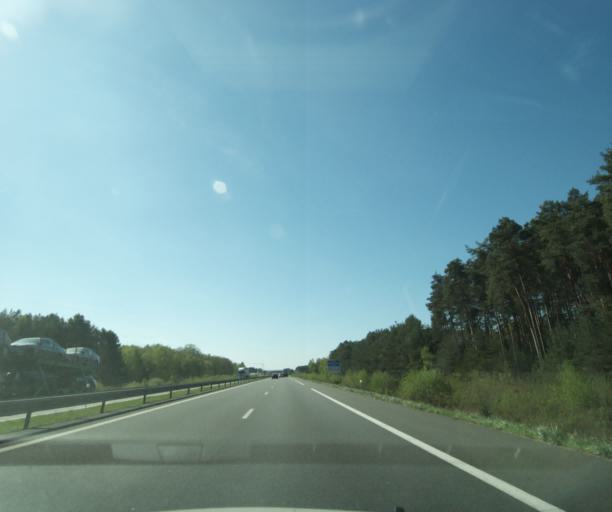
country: FR
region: Centre
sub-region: Departement du Loir-et-Cher
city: Theillay
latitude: 47.3559
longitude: 2.0511
